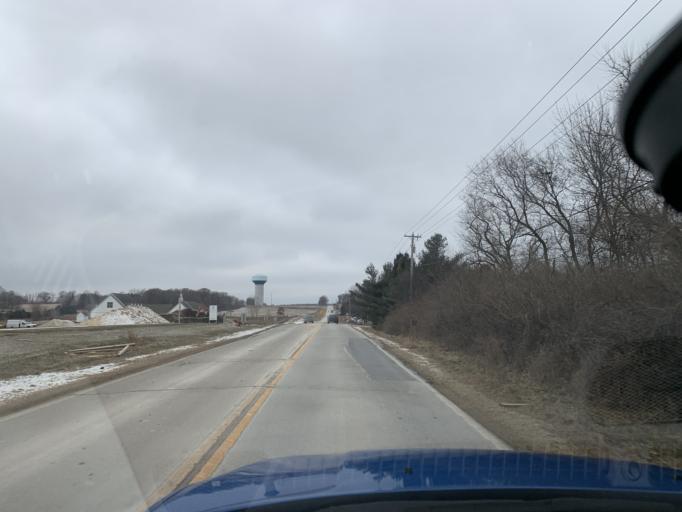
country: US
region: Wisconsin
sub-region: Dane County
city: Middleton
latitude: 43.0748
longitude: -89.5581
